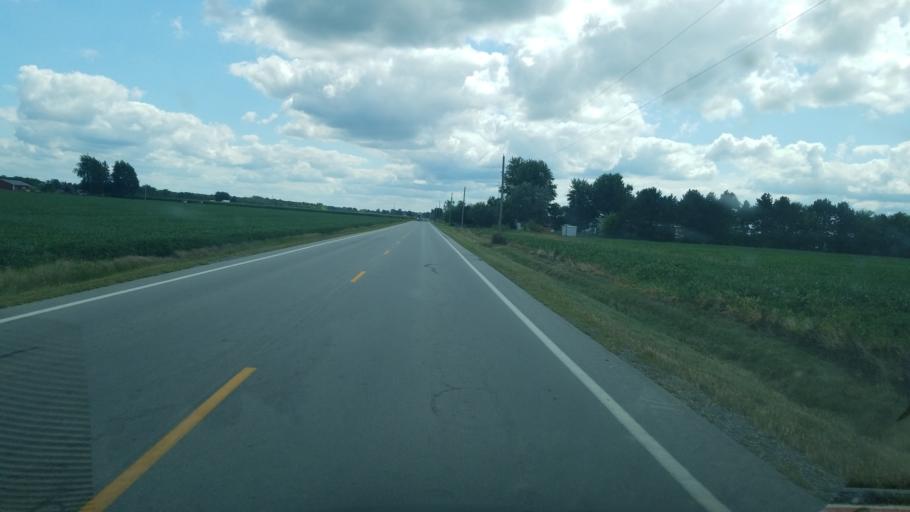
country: US
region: Ohio
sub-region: Allen County
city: Elida
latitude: 40.8458
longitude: -84.1379
